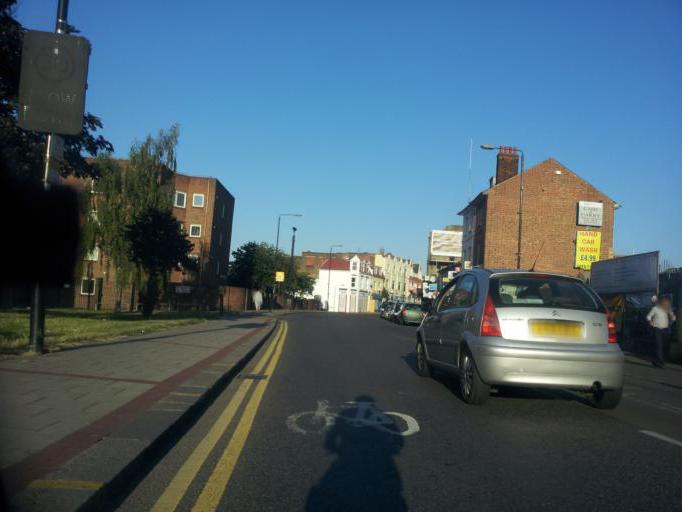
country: GB
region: England
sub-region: Greater London
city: Abbey Wood
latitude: 51.4890
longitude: 0.0875
